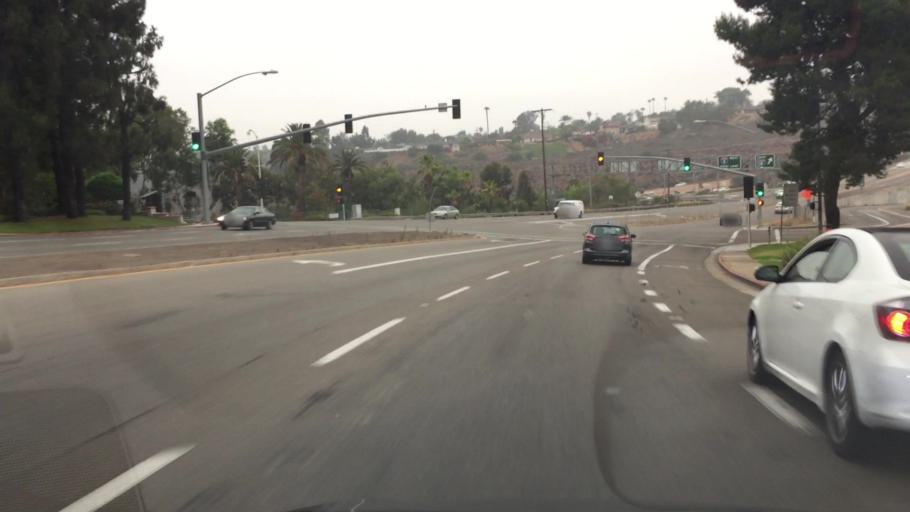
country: US
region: California
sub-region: San Diego County
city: La Mesa
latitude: 32.7762
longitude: -117.0678
